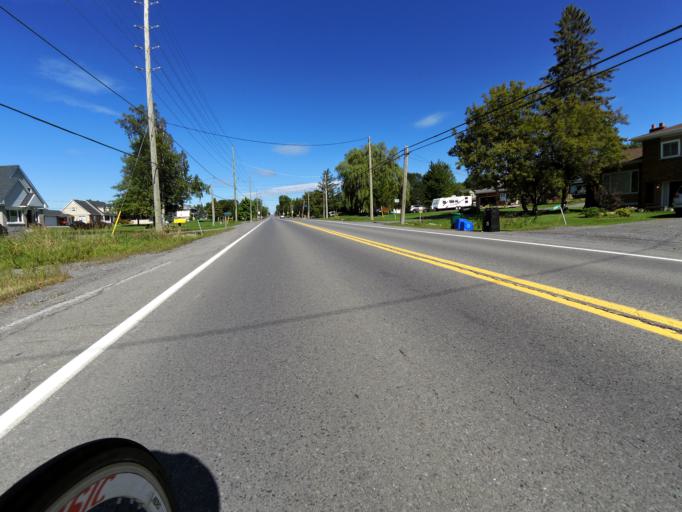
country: CA
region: Ontario
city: Bells Corners
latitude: 45.2646
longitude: -75.8283
